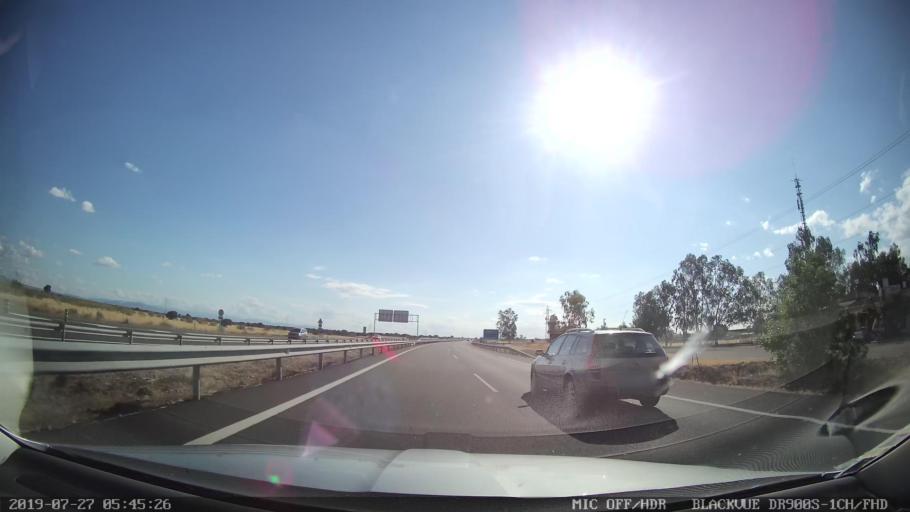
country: ES
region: Castille-La Mancha
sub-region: Province of Toledo
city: Velada
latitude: 39.9420
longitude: -4.9548
